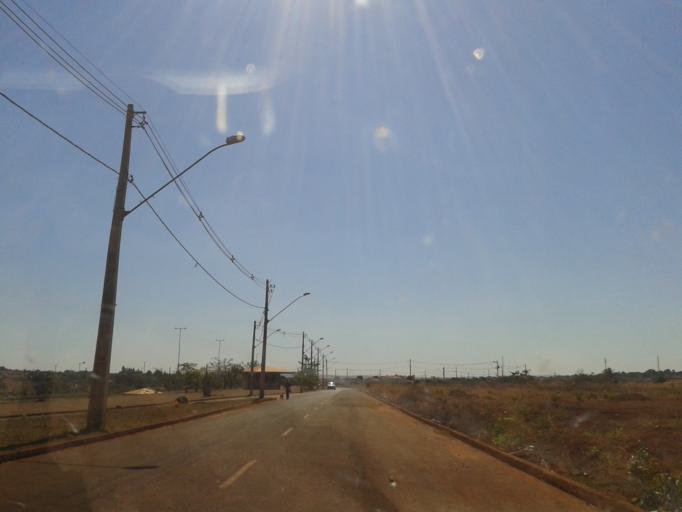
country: BR
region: Minas Gerais
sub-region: Ituiutaba
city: Ituiutaba
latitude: -19.0027
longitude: -49.4754
